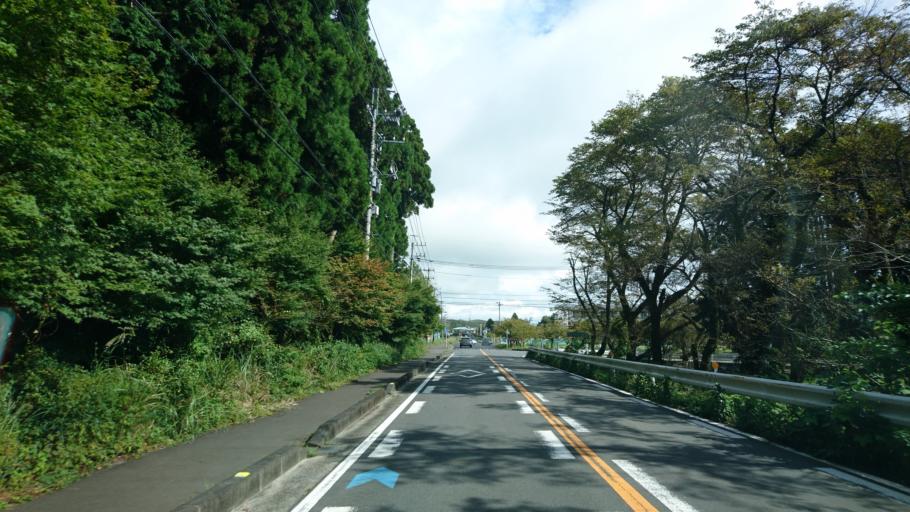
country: JP
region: Shizuoka
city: Gotemba
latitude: 35.2569
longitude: 138.8592
